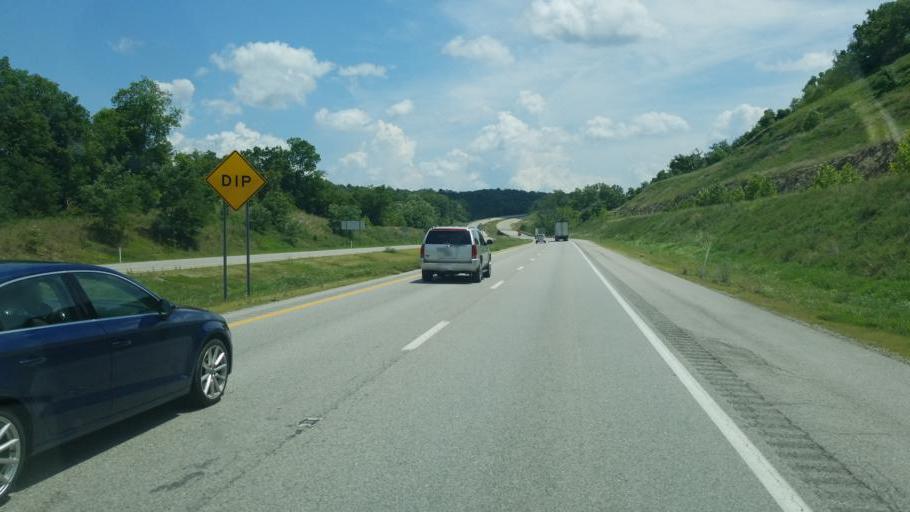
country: US
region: West Virginia
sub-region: Mason County
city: Point Pleasant
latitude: 38.7806
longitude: -82.0693
